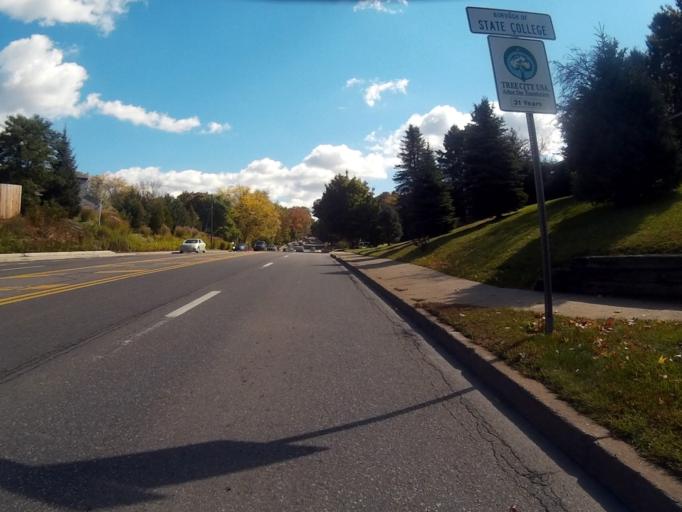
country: US
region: Pennsylvania
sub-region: Centre County
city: State College
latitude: 40.8009
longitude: -77.8792
